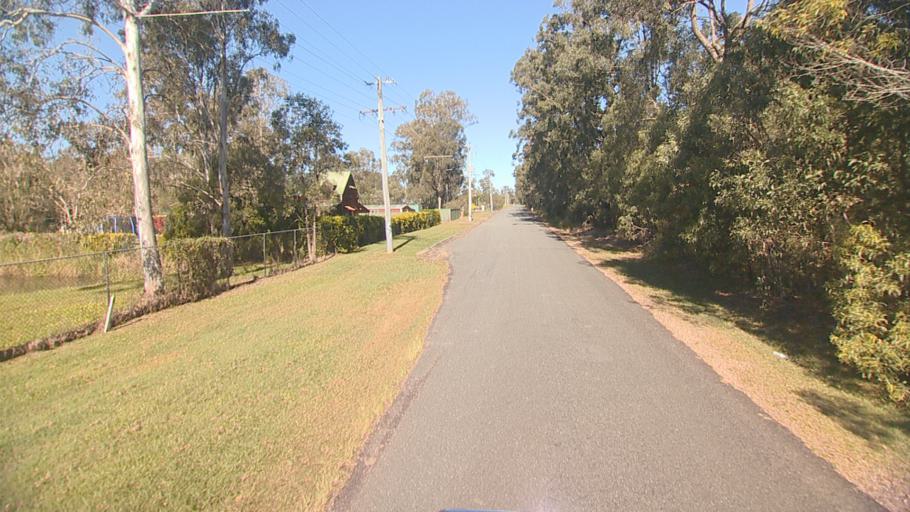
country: AU
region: Queensland
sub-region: Logan
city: Park Ridge South
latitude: -27.6973
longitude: 153.0042
